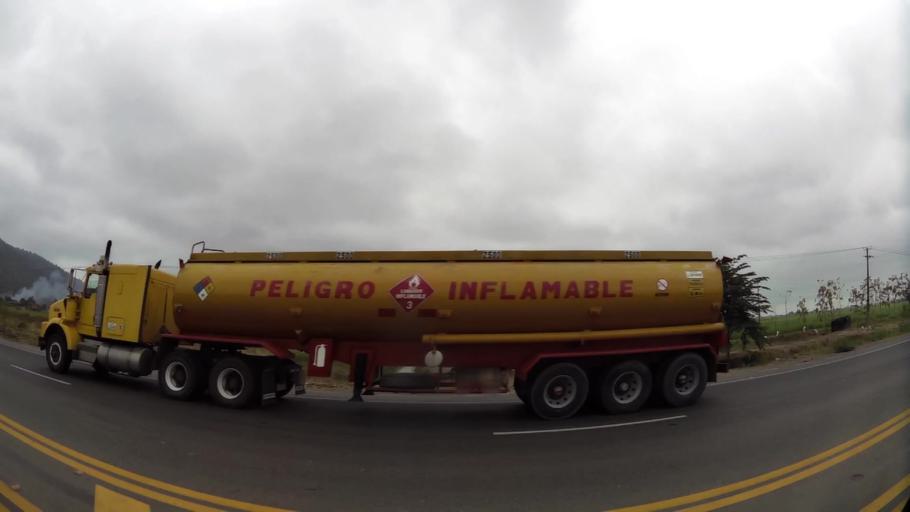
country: EC
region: Guayas
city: Naranjal
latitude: -2.4756
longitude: -79.6197
